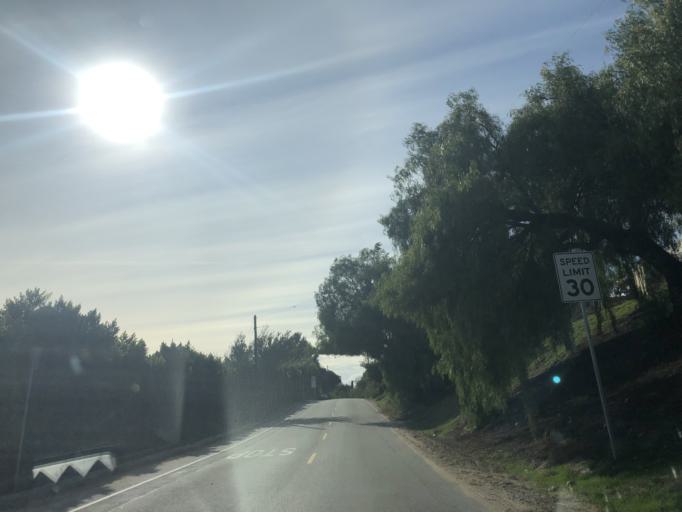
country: US
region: California
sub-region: Los Angeles County
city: San Fernando
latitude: 34.2810
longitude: -118.3724
